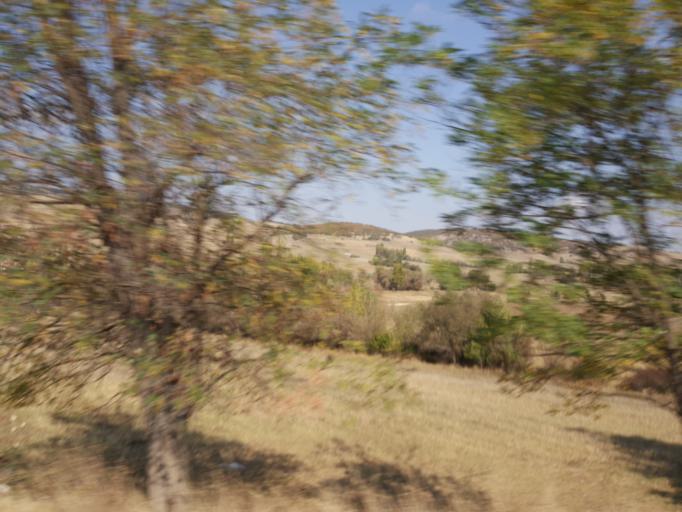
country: TR
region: Corum
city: Bogazkale
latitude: 40.1568
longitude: 34.6454
